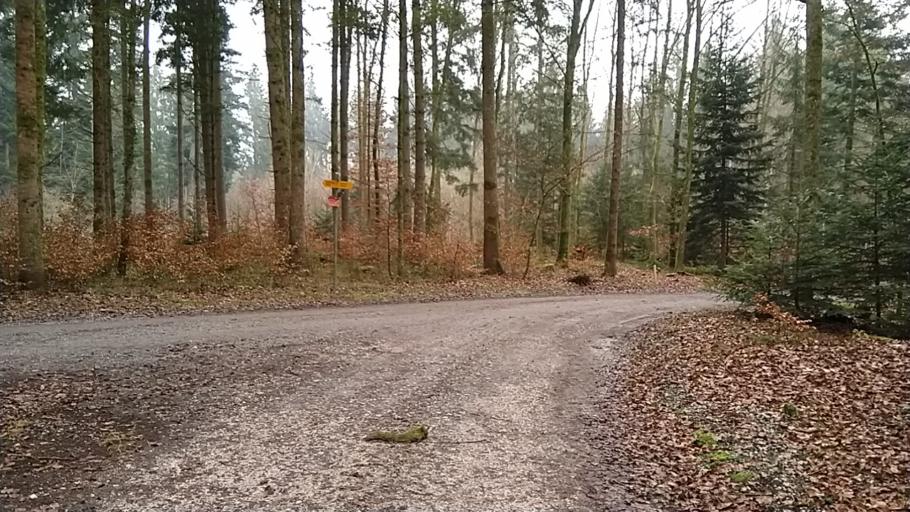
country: CH
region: Bern
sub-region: Bern-Mittelland District
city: Kirchlindach
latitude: 46.9628
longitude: 7.4129
